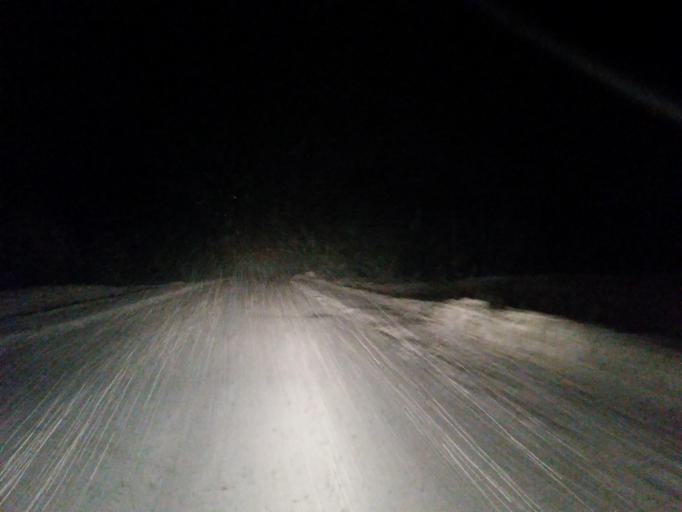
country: SE
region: Norrbotten
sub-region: Pitea Kommun
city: Pitea
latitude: 65.2688
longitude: 21.5375
